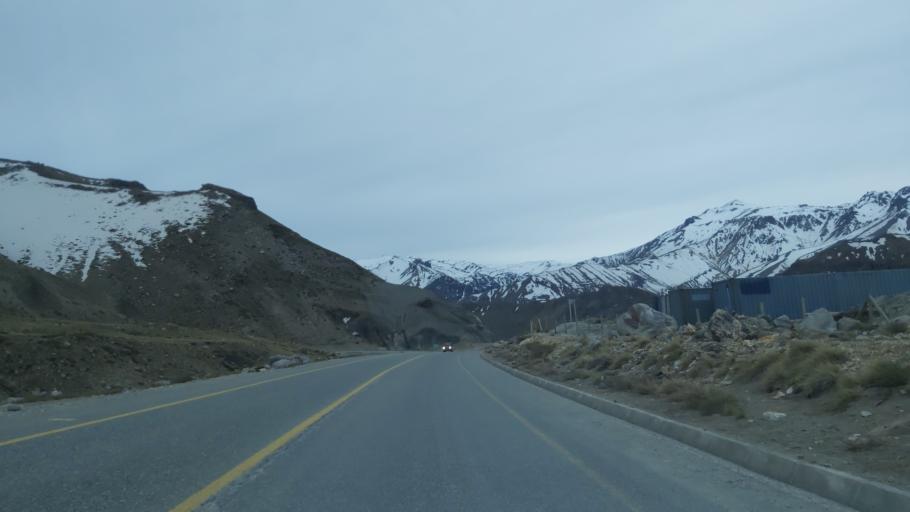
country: CL
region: Maule
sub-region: Provincia de Linares
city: Colbun
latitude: -35.9654
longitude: -70.5716
